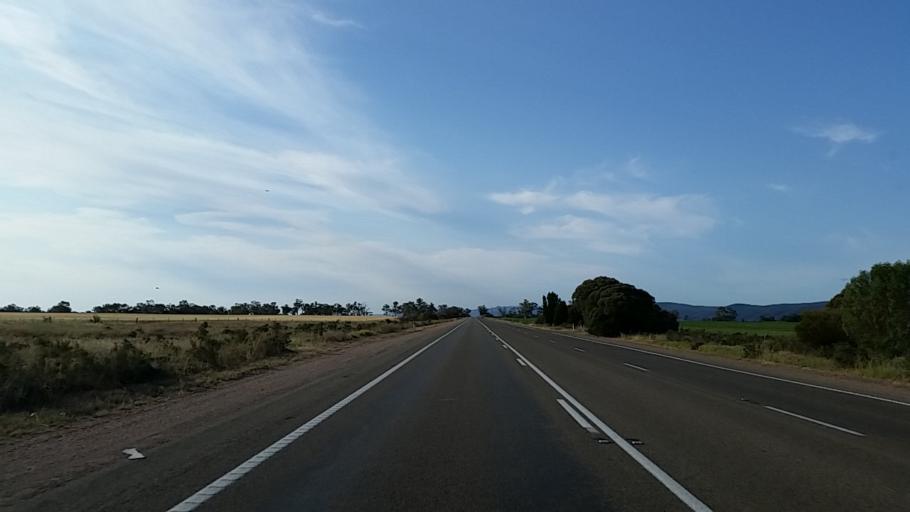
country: AU
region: South Australia
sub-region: Port Pirie City and Dists
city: Solomontown
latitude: -33.1409
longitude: 138.0683
